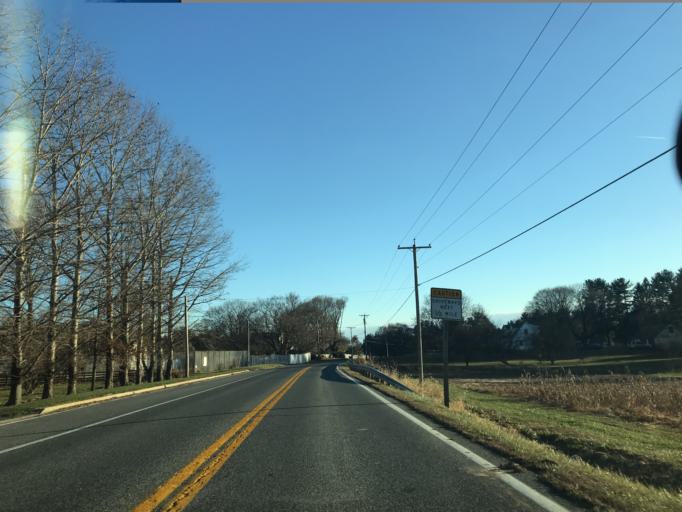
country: US
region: Maryland
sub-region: Harford County
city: Jarrettsville
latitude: 39.6054
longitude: -76.5129
